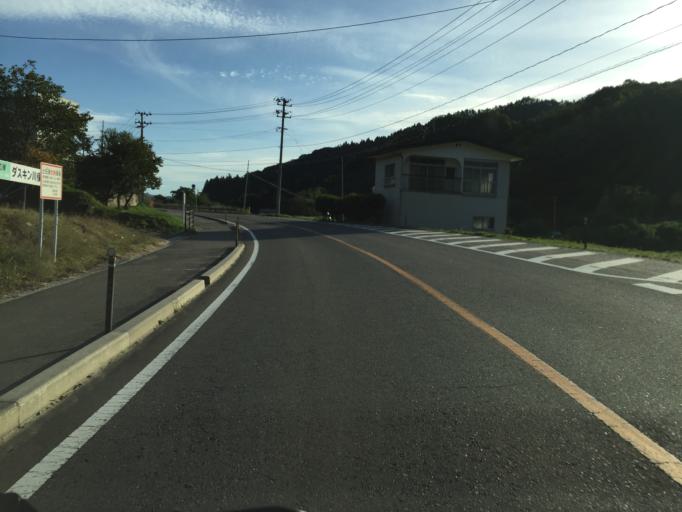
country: JP
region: Fukushima
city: Hobaramachi
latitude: 37.6821
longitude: 140.6164
